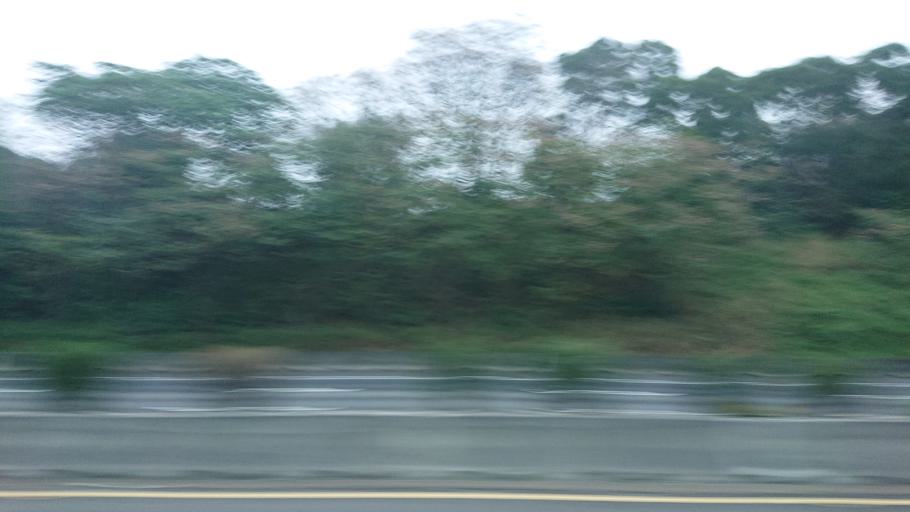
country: TW
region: Taiwan
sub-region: Hsinchu
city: Hsinchu
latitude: 24.7040
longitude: 120.9278
